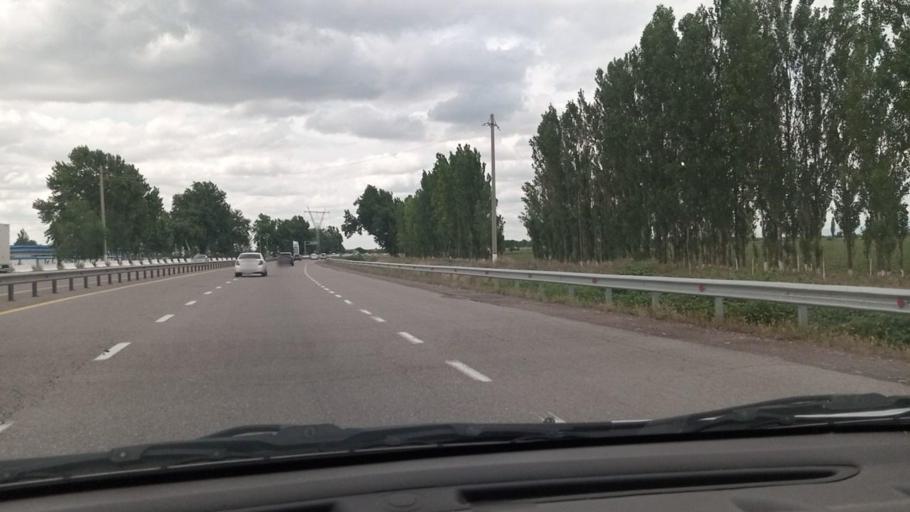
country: UZ
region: Toshkent Shahri
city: Bektemir
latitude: 41.1842
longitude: 69.4049
